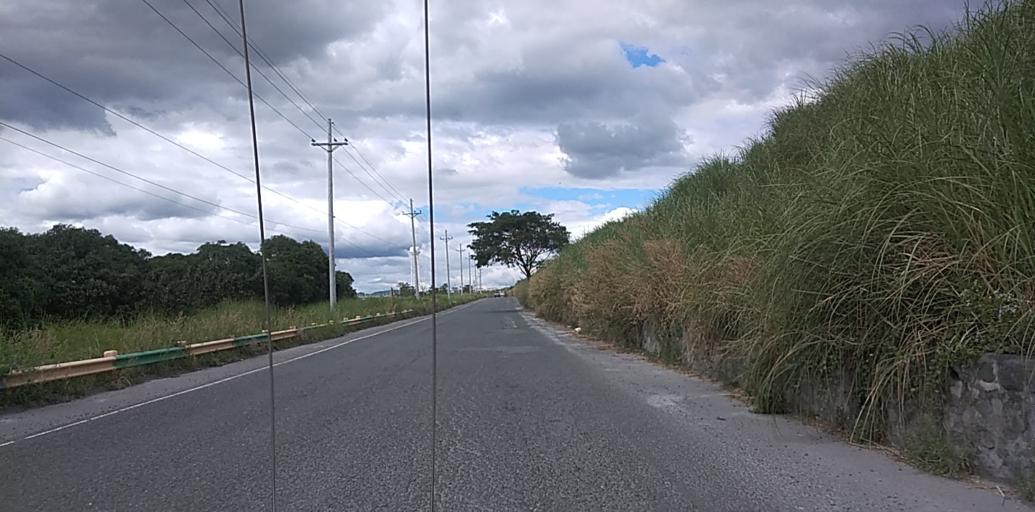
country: PH
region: Central Luzon
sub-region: Province of Pampanga
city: Dolores
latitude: 15.1072
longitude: 120.5201
